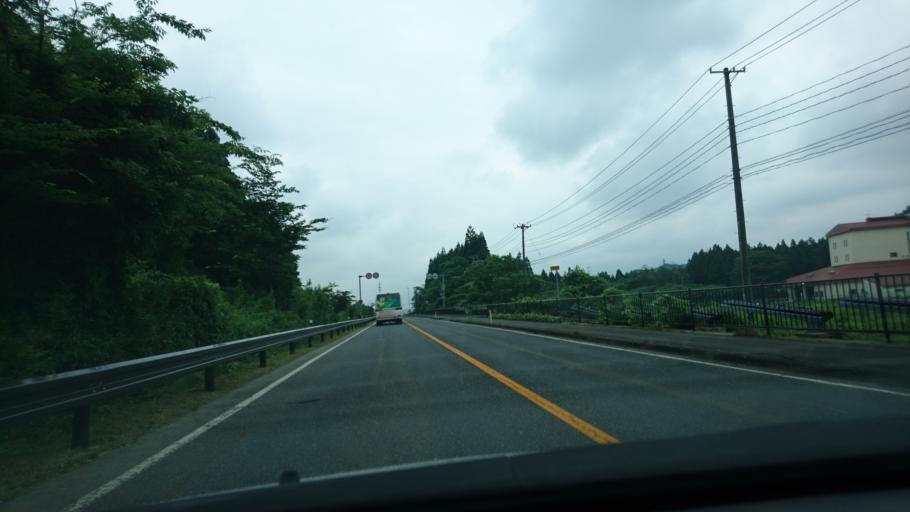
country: JP
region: Miyagi
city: Furukawa
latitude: 38.7171
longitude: 140.8054
